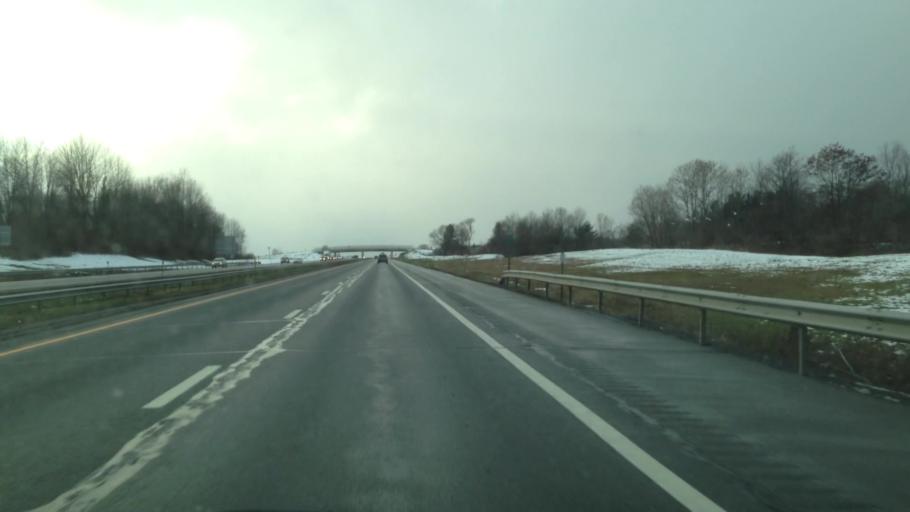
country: US
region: New York
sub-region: Montgomery County
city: Amsterdam
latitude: 42.9278
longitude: -74.2183
